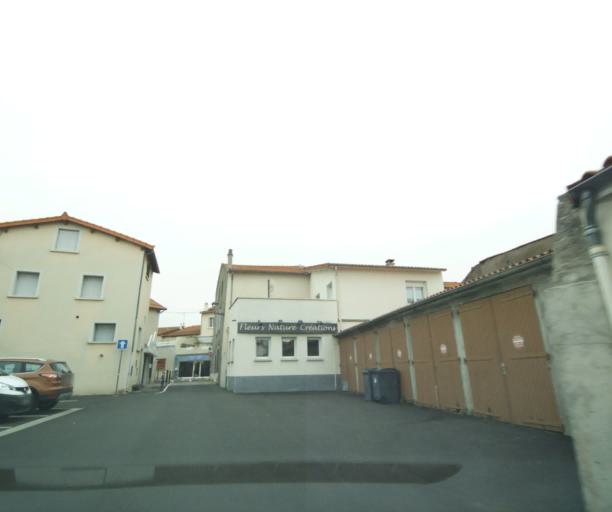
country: FR
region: Auvergne
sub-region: Departement du Puy-de-Dome
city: Gerzat
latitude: 45.8235
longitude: 3.1446
